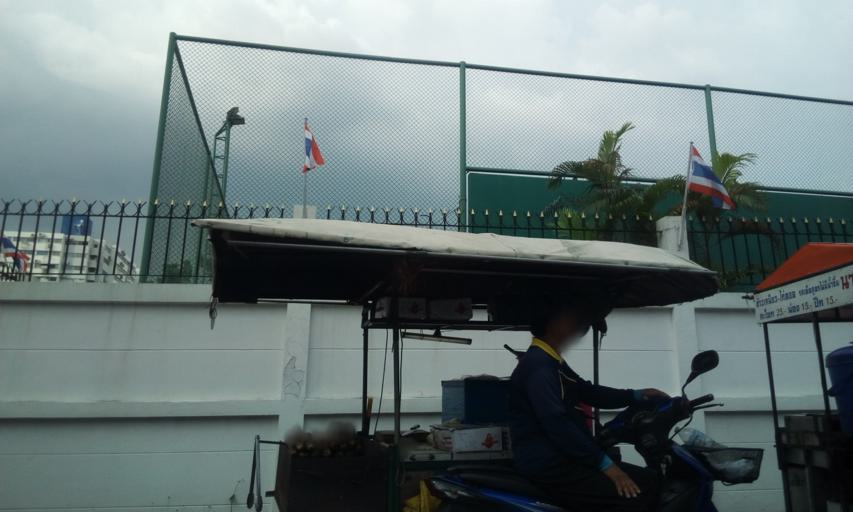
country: TH
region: Bangkok
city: Don Mueang
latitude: 13.9136
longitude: 100.5552
